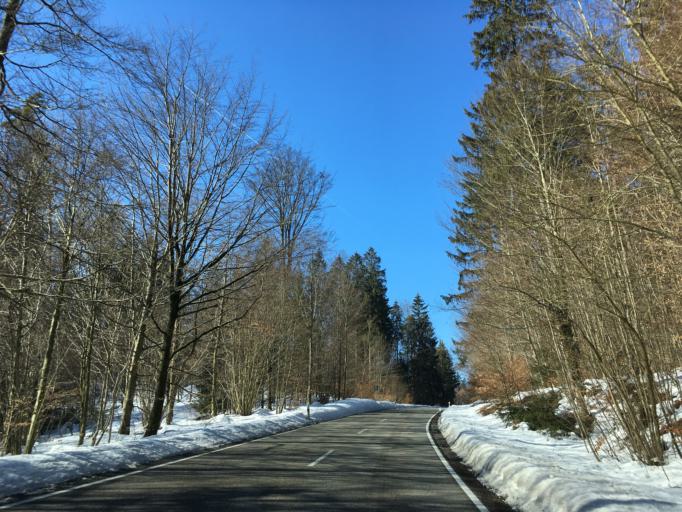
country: DE
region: Bavaria
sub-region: Upper Bavaria
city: Maitenbeth
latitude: 48.1271
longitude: 12.0829
